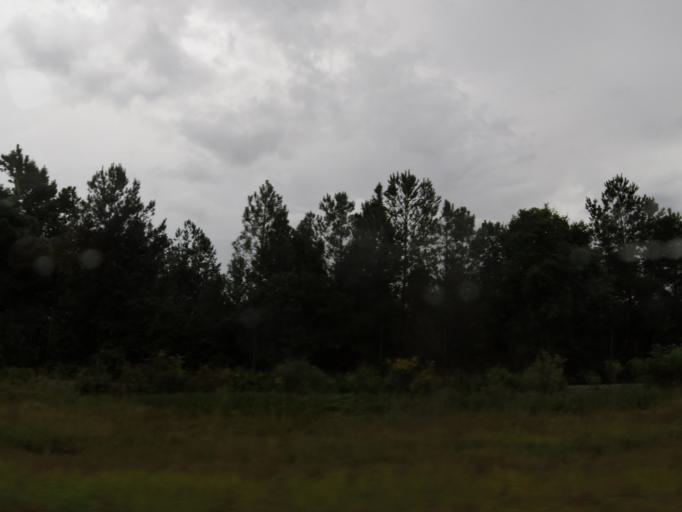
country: US
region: Georgia
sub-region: Wayne County
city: Jesup
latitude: 31.4596
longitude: -81.7082
